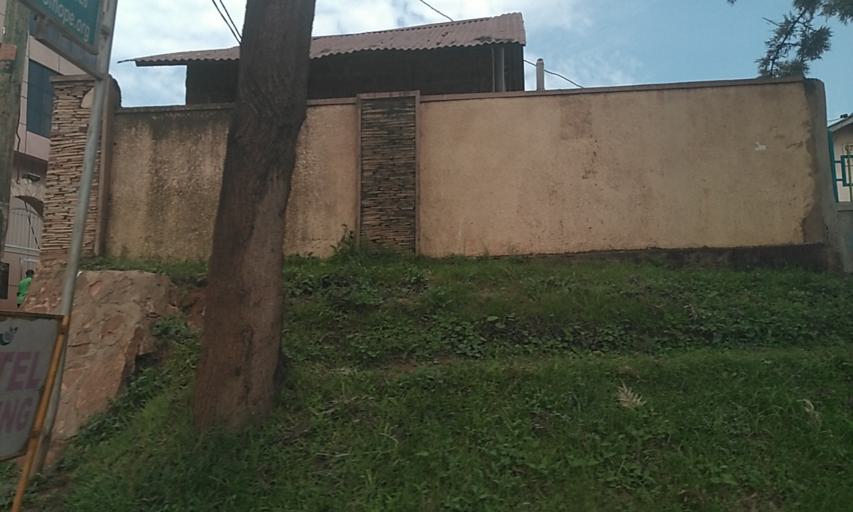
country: UG
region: Central Region
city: Kampala Central Division
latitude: 0.3018
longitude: 32.5390
